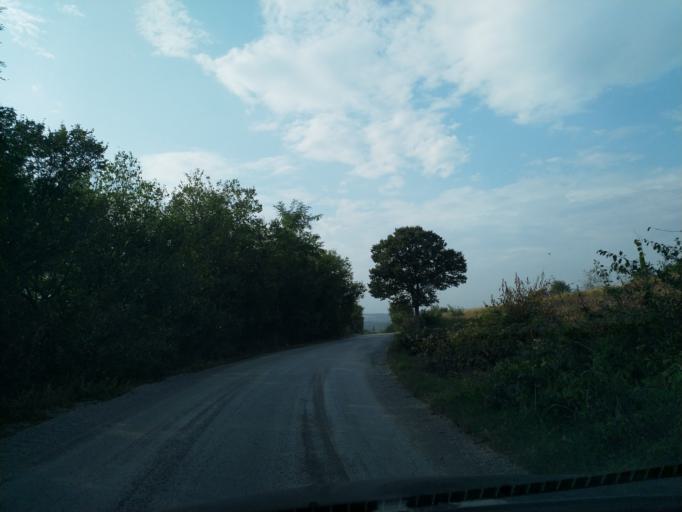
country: RS
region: Central Serbia
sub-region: Pomoravski Okrug
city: Paracin
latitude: 43.8418
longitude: 21.5308
